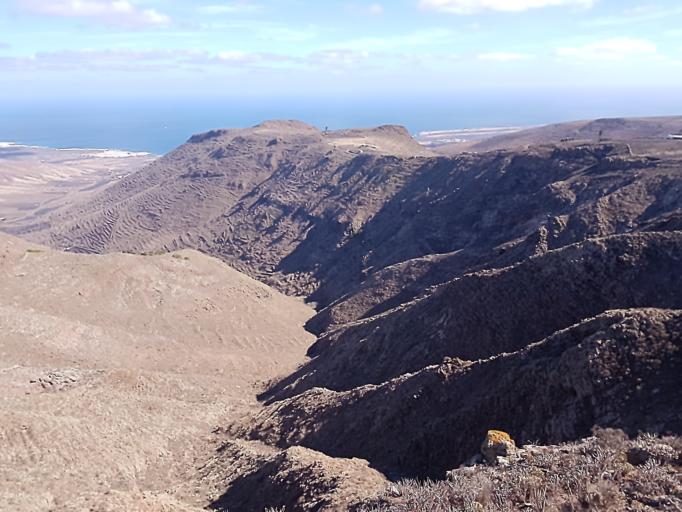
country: ES
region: Canary Islands
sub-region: Provincia de Las Palmas
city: Haria
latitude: 29.1227
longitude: -13.5155
